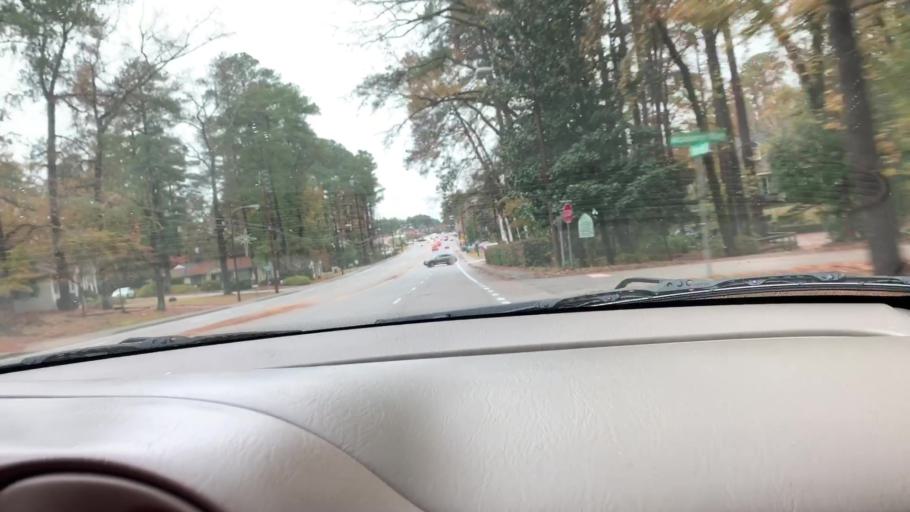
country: US
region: South Carolina
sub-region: Richland County
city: Forest Acres
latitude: 34.0224
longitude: -80.9664
